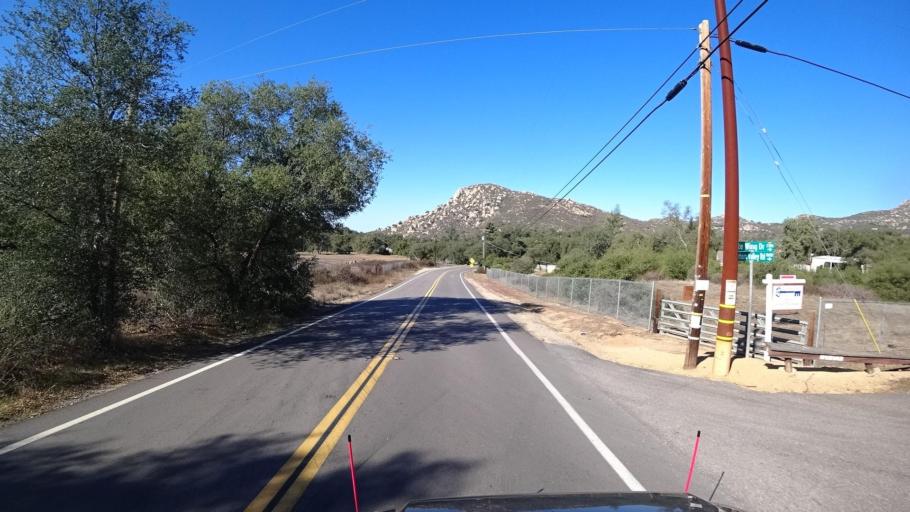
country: US
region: California
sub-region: San Diego County
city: Jamul
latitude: 32.6782
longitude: -116.7483
